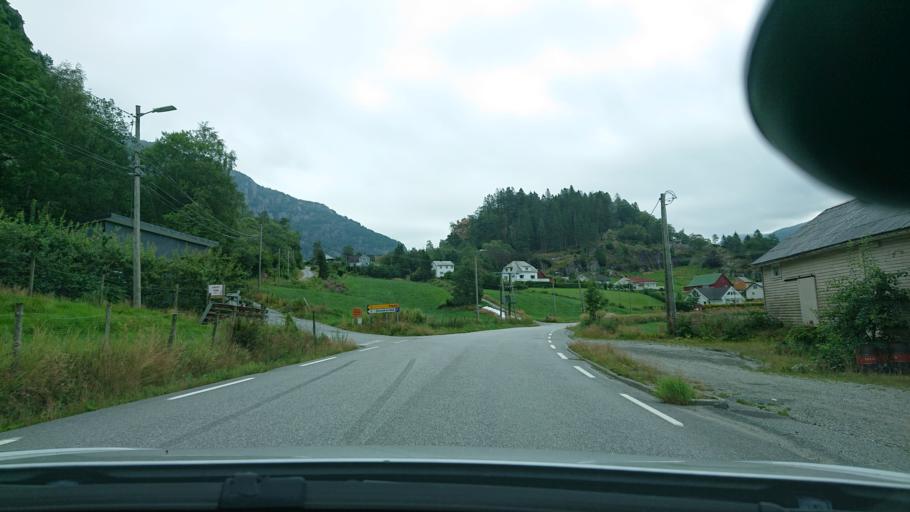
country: NO
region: Rogaland
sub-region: Hjelmeland
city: Hjelmelandsvagen
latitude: 59.2343
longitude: 6.1874
